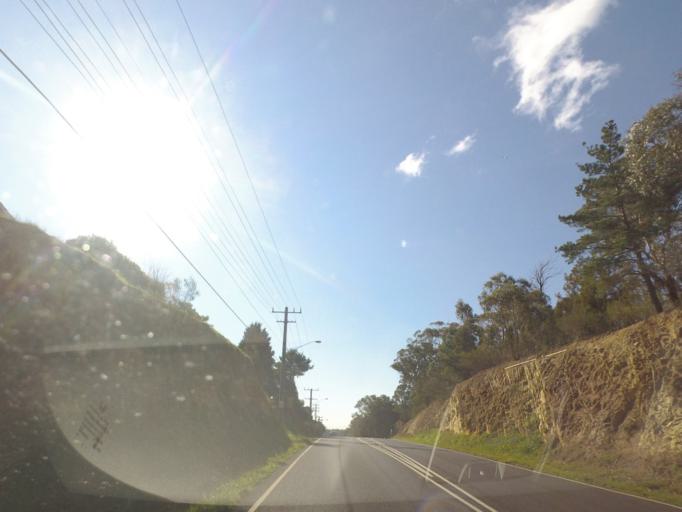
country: AU
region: Victoria
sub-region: Manningham
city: Donvale
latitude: -37.7739
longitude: 145.1832
